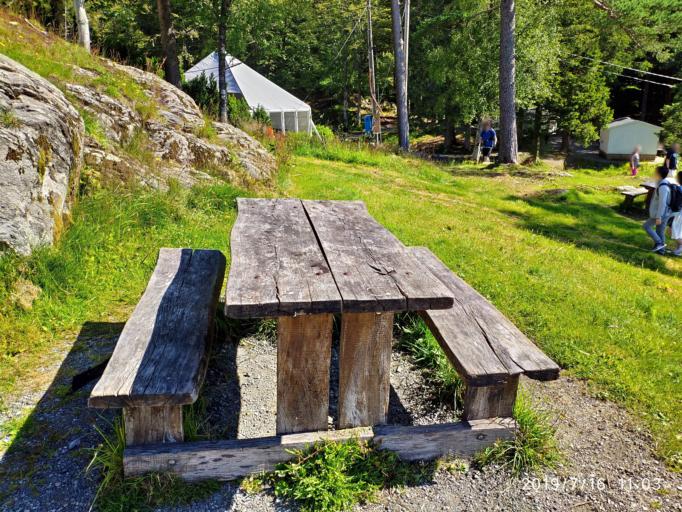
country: NO
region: Hordaland
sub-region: Bergen
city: Bergen
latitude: 60.3940
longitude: 5.3441
